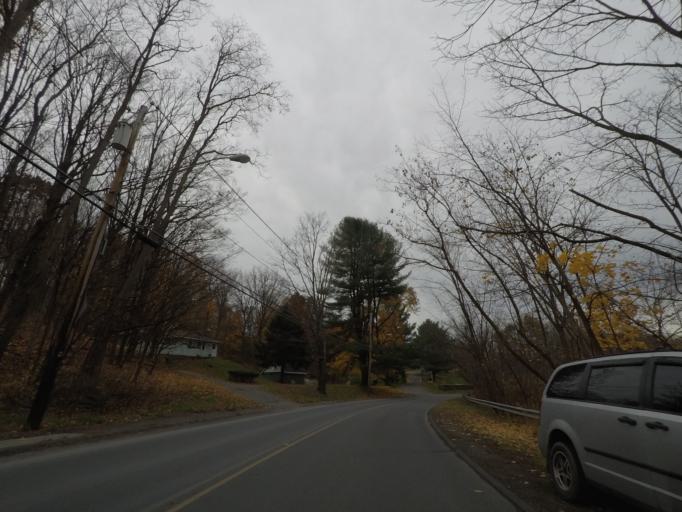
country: US
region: New York
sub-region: Rensselaer County
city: Troy
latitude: 42.7234
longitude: -73.6654
